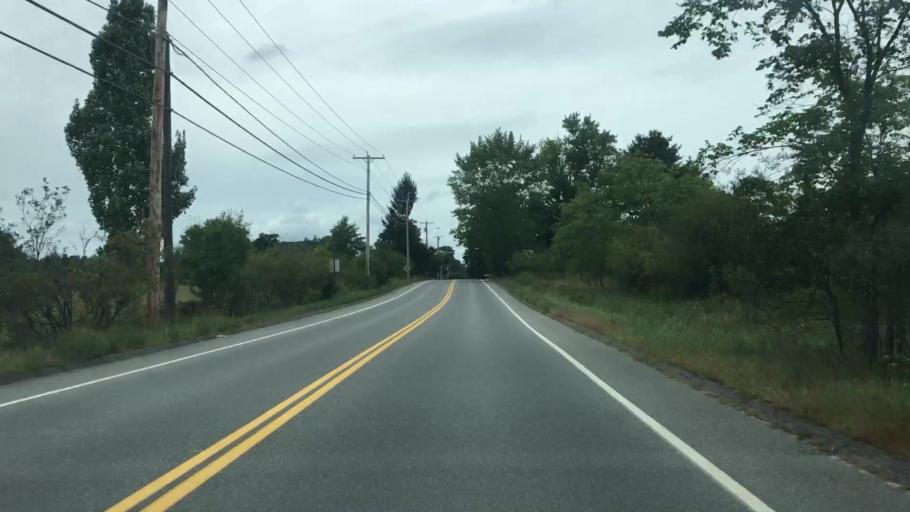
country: US
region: Maine
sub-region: Cumberland County
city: Yarmouth
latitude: 43.8259
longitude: -70.1932
